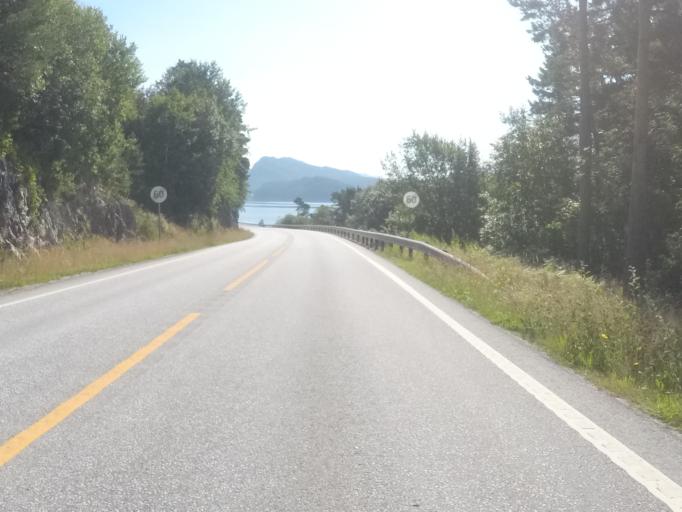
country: NO
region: Sogn og Fjordane
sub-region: Flora
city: Floro
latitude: 61.6018
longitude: 5.1474
